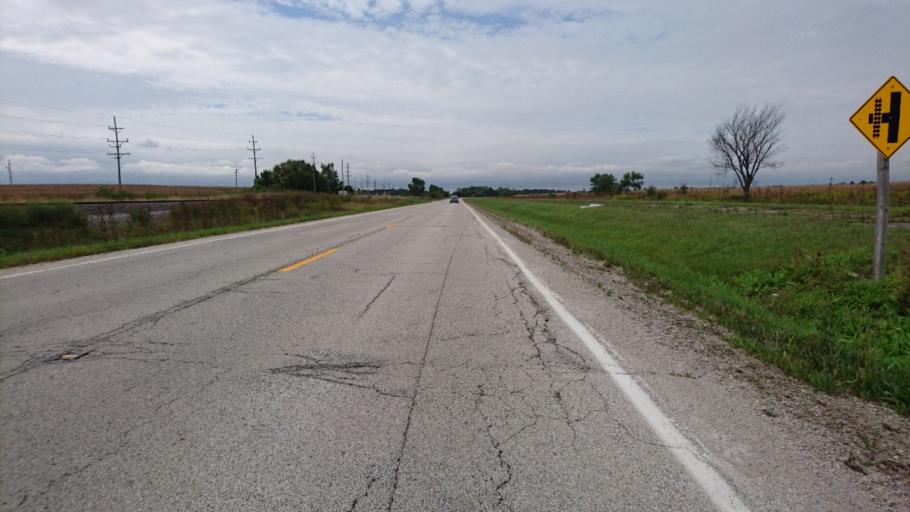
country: US
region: Illinois
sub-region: Livingston County
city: Odell
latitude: 41.0221
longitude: -88.5078
